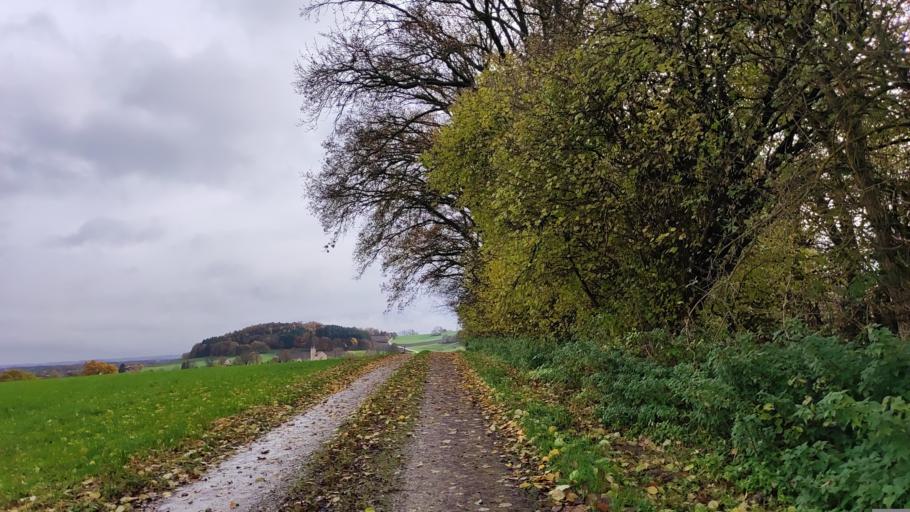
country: DE
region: Bavaria
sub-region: Swabia
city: Dinkelscherben
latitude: 48.3466
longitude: 10.5488
